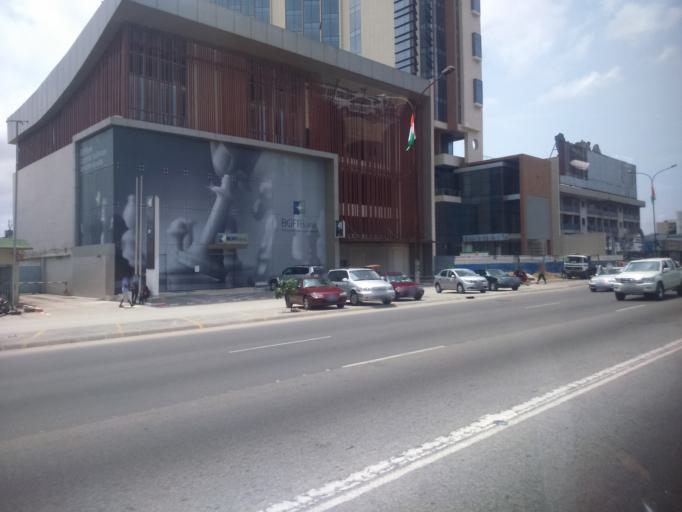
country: CI
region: Lagunes
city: Abidjan
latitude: 5.2992
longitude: -3.9872
